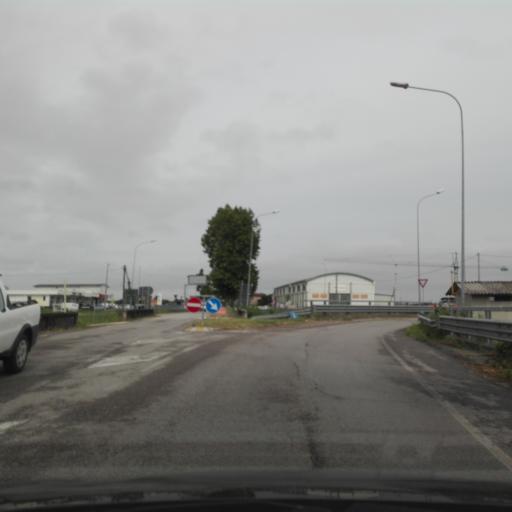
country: IT
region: Veneto
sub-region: Provincia di Rovigo
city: Rovigo
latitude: 45.0768
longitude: 11.7670
